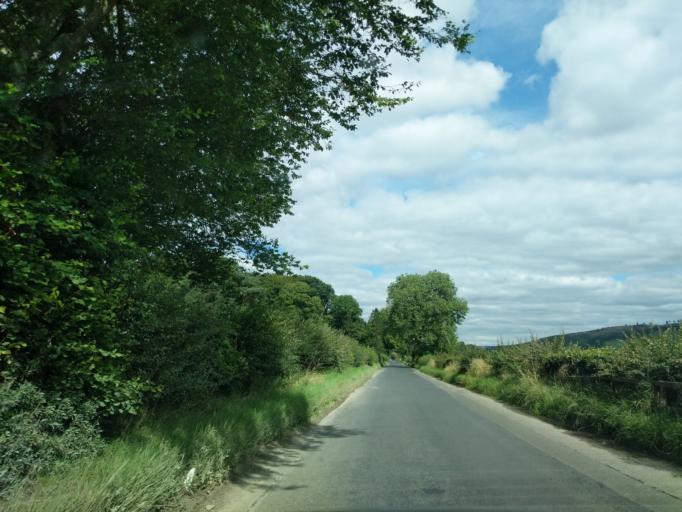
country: GB
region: Scotland
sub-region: The Scottish Borders
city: Peebles
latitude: 55.6212
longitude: -3.3027
